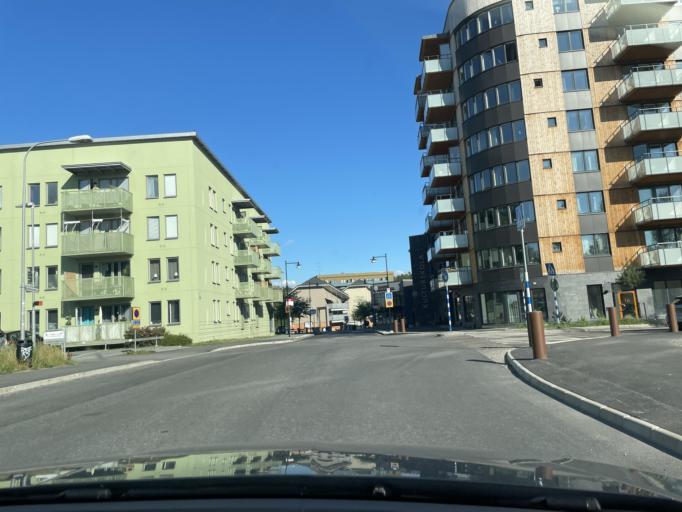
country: SE
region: Stockholm
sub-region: Sigtuna Kommun
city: Marsta
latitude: 59.6221
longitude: 17.8550
